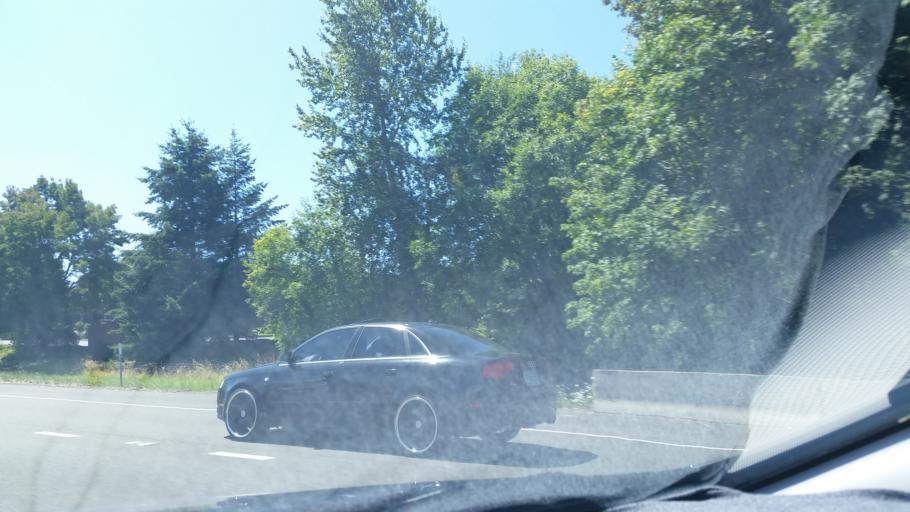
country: US
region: Oregon
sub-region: Washington County
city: Tualatin
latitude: 45.3791
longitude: -122.7542
